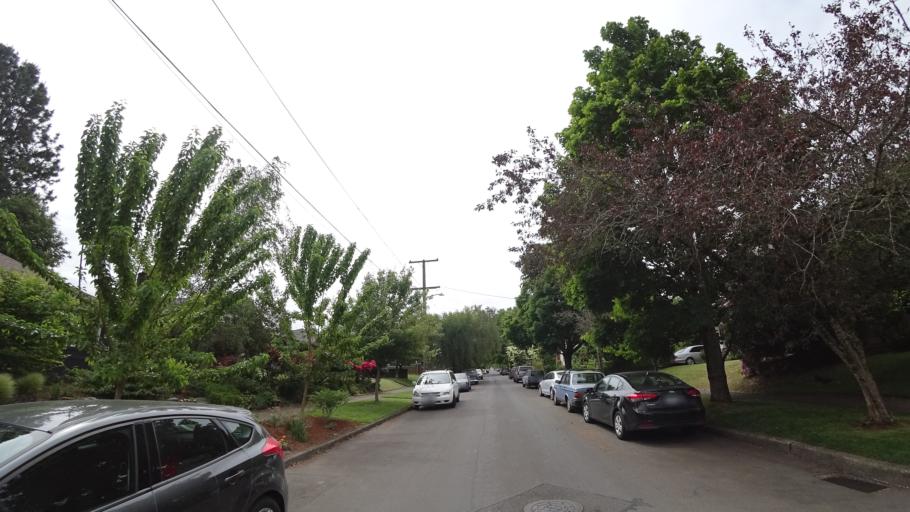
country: US
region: Oregon
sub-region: Multnomah County
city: Portland
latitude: 45.5713
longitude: -122.6403
